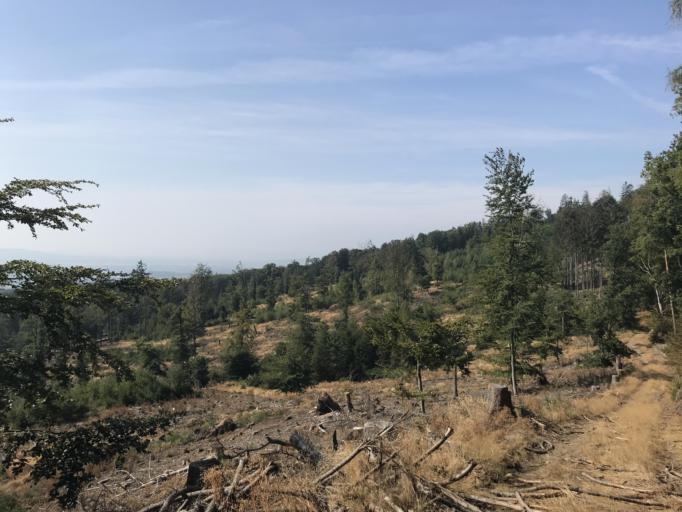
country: DE
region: Rheinland-Pfalz
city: Oestrich-Winkel
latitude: 50.0429
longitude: 8.0126
